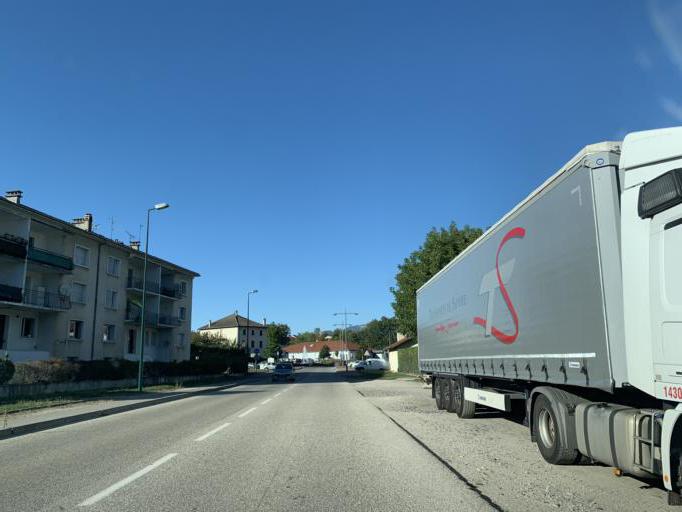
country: FR
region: Rhone-Alpes
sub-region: Departement de l'Ain
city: Belley
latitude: 45.7571
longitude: 5.6966
